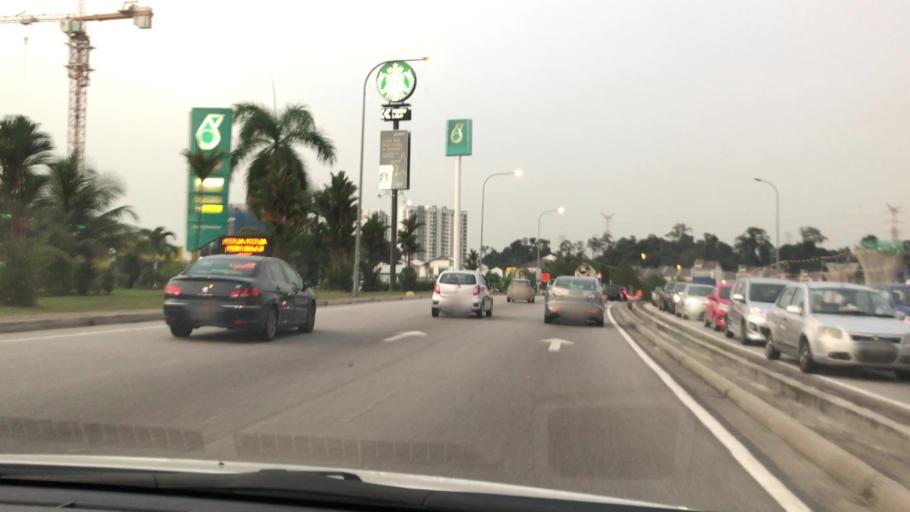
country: MY
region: Putrajaya
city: Putrajaya
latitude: 2.9938
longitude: 101.6760
